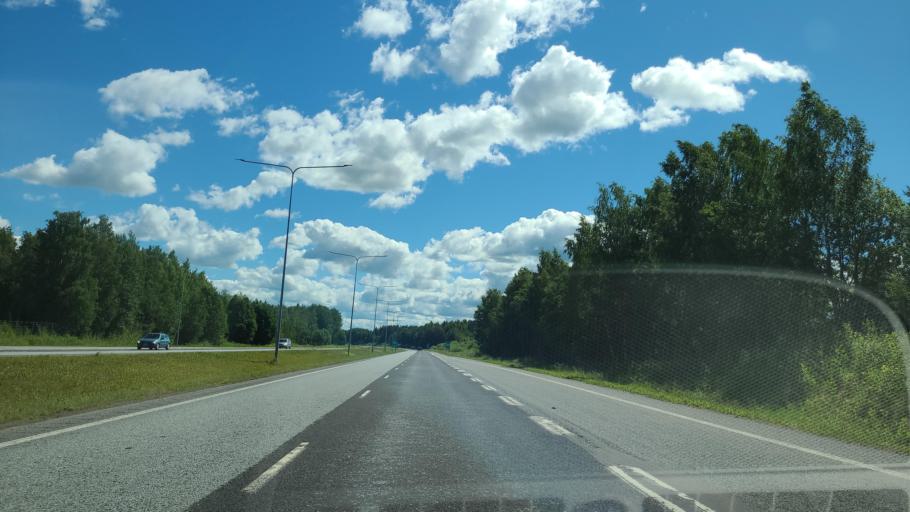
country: FI
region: Ostrobothnia
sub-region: Vaasa
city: Ristinummi
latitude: 63.0275
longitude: 21.7606
